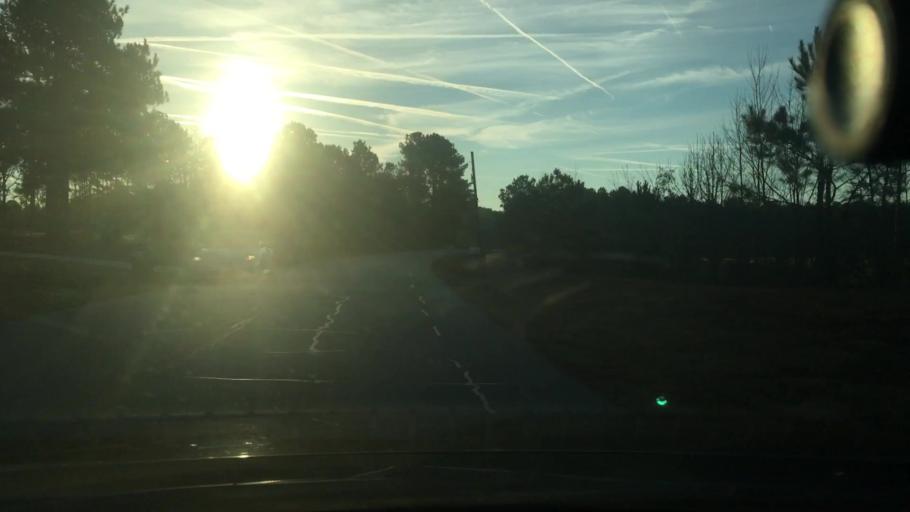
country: US
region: Georgia
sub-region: Coweta County
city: Senoia
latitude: 33.3120
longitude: -84.4731
